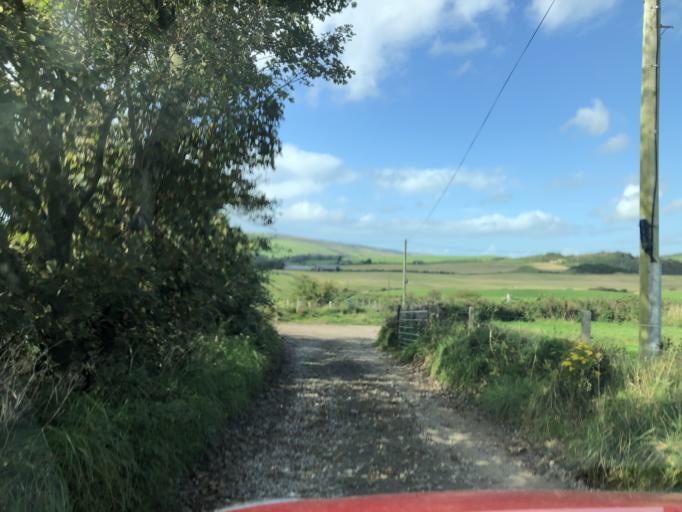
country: GB
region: Scotland
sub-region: Argyll and Bute
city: Campbeltown
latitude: 55.3189
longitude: -5.6144
